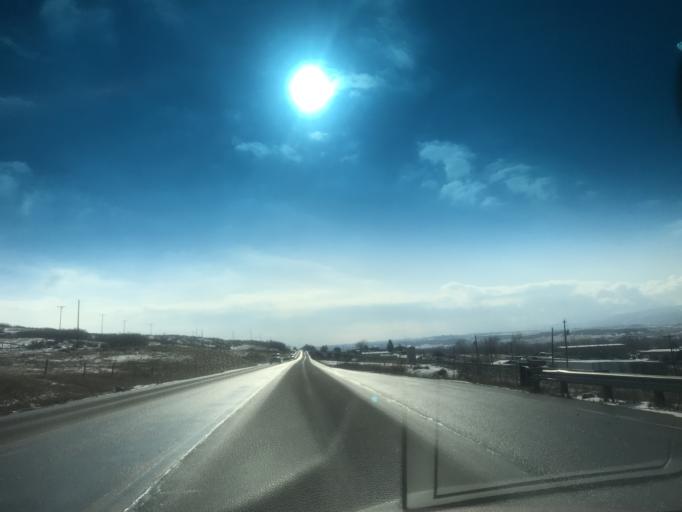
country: US
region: Colorado
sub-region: Douglas County
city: Highlands Ranch
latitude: 39.4694
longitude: -104.9883
